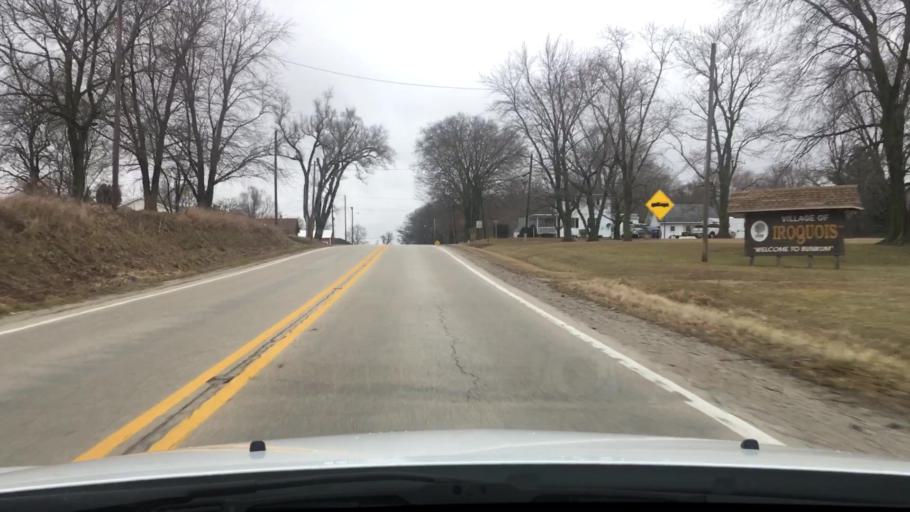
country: US
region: Illinois
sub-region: Iroquois County
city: Sheldon
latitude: 40.8250
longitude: -87.5816
